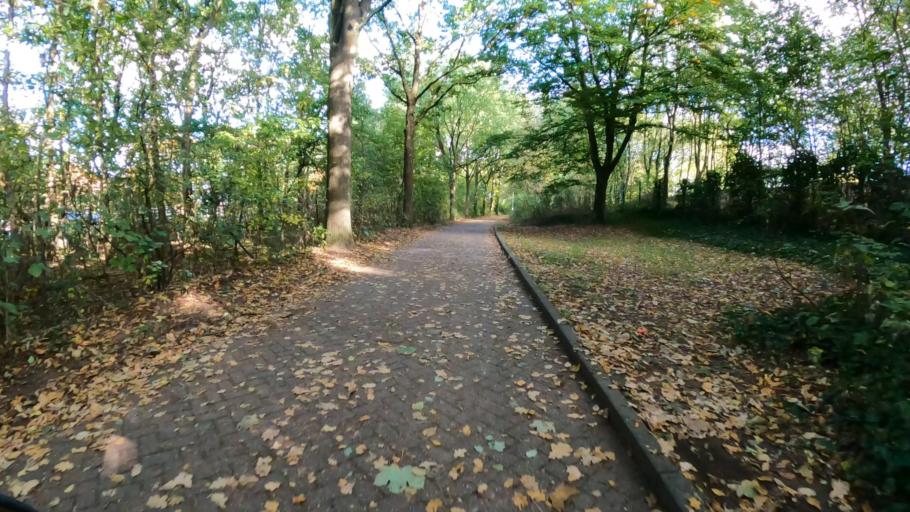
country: DE
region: Schleswig-Holstein
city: Henstedt-Ulzburg
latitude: 53.7920
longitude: 9.9885
